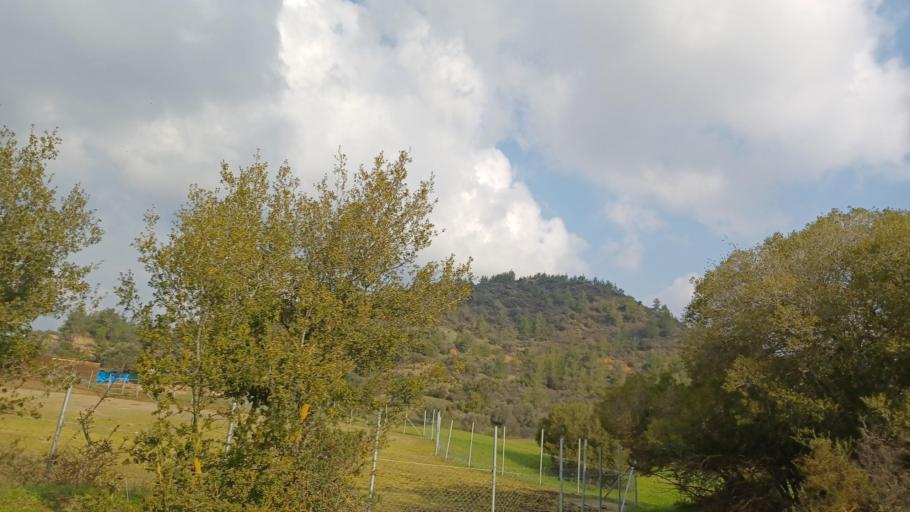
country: CY
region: Pafos
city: Polis
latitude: 34.9963
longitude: 32.5340
